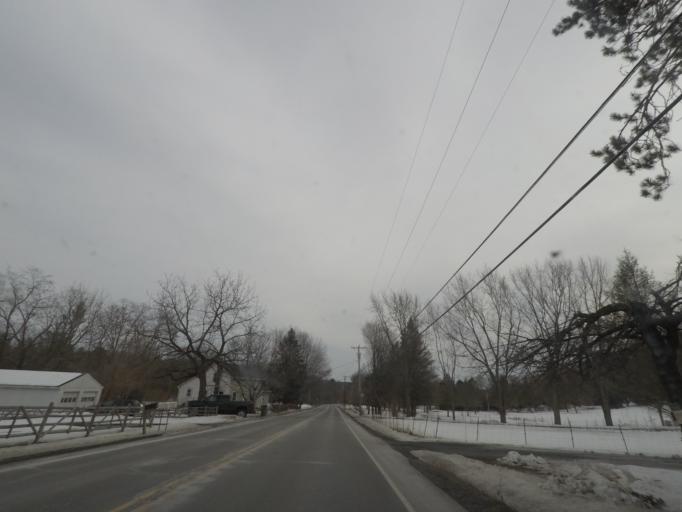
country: US
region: New York
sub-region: Albany County
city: Voorheesville
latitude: 42.5914
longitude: -73.9853
